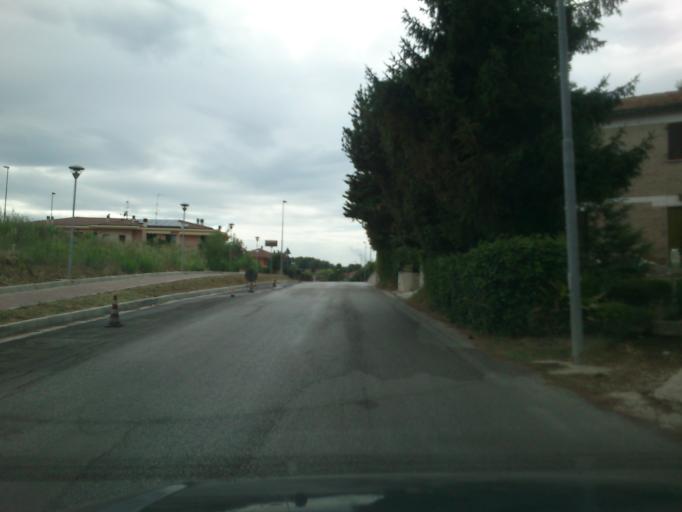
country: IT
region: The Marches
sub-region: Provincia di Pesaro e Urbino
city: Lucrezia
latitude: 43.7728
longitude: 12.9303
